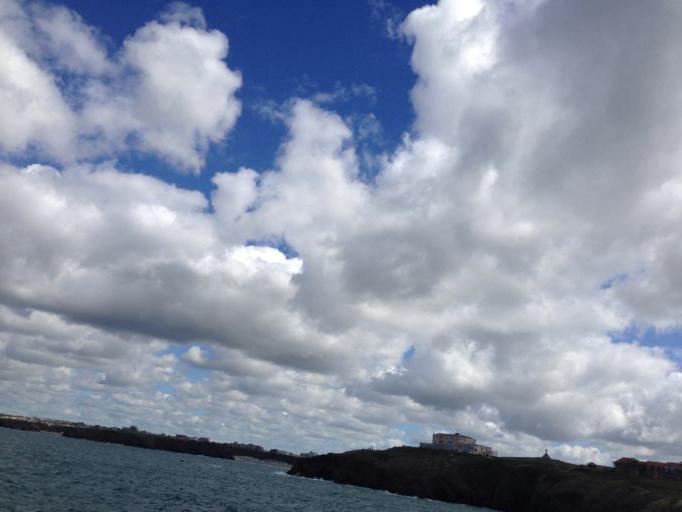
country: GB
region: England
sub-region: Cornwall
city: Newquay
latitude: 50.4233
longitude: -5.0973
